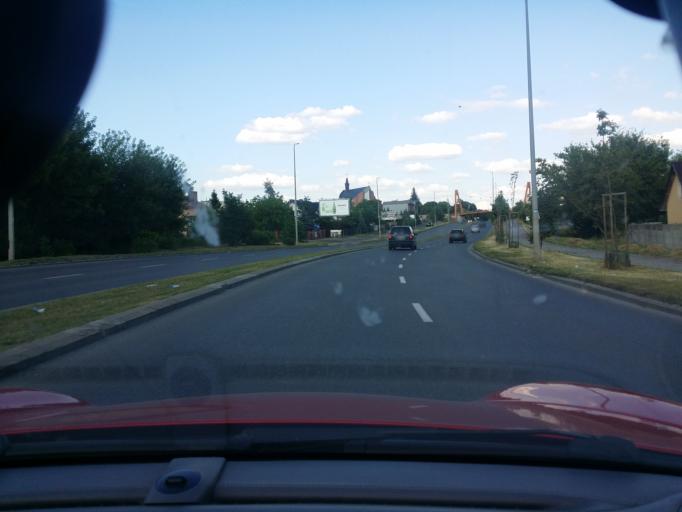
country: PL
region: Masovian Voivodeship
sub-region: Radom
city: Radom
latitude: 51.4129
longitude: 21.1457
